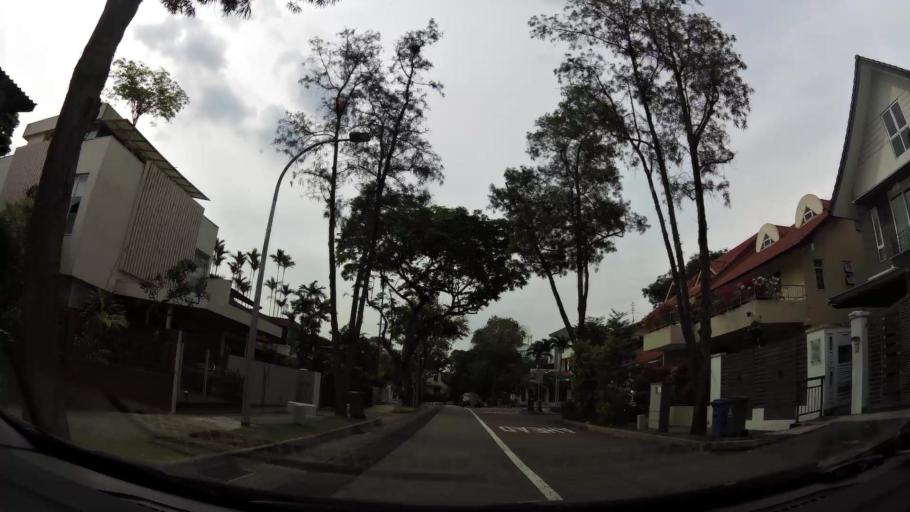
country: SG
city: Singapore
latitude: 1.3258
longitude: 103.7940
